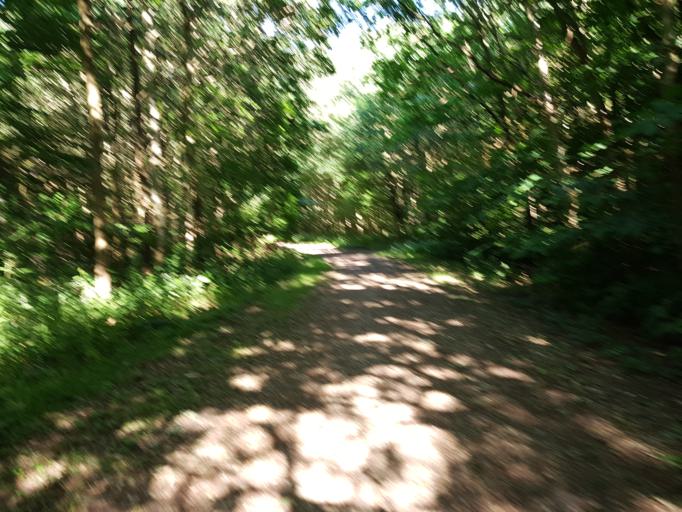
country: DK
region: South Denmark
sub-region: Esbjerg Kommune
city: Esbjerg
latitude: 55.4862
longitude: 8.5162
